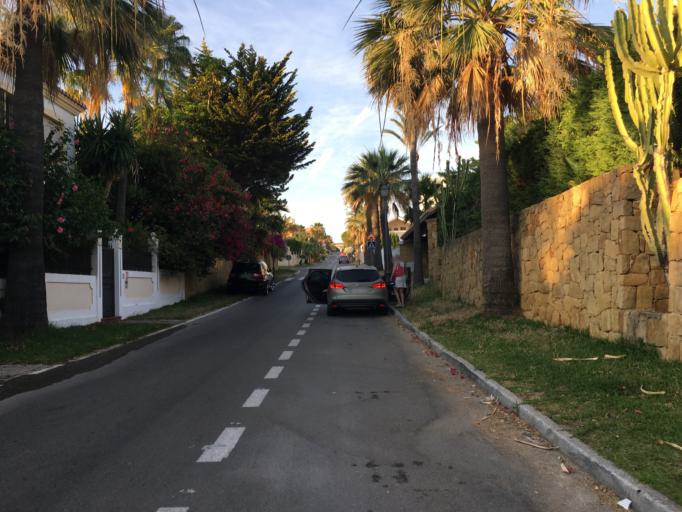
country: ES
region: Andalusia
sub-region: Provincia de Malaga
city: Marbella
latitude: 36.4998
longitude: -4.8144
